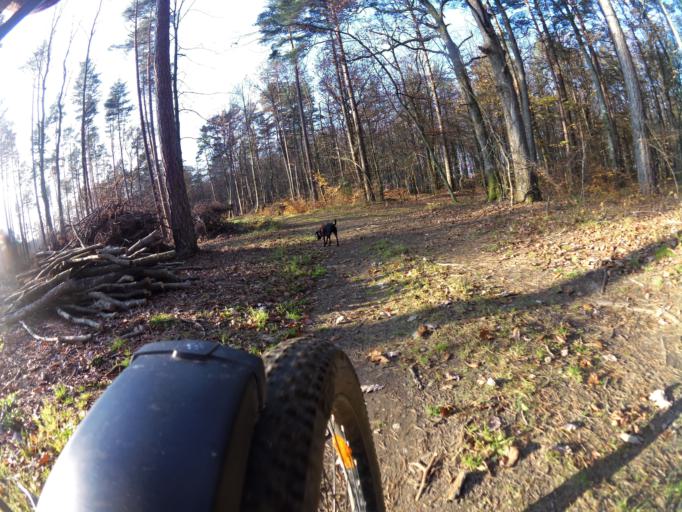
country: PL
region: Pomeranian Voivodeship
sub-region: Powiat pucki
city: Krokowa
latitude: 54.7295
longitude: 18.2056
